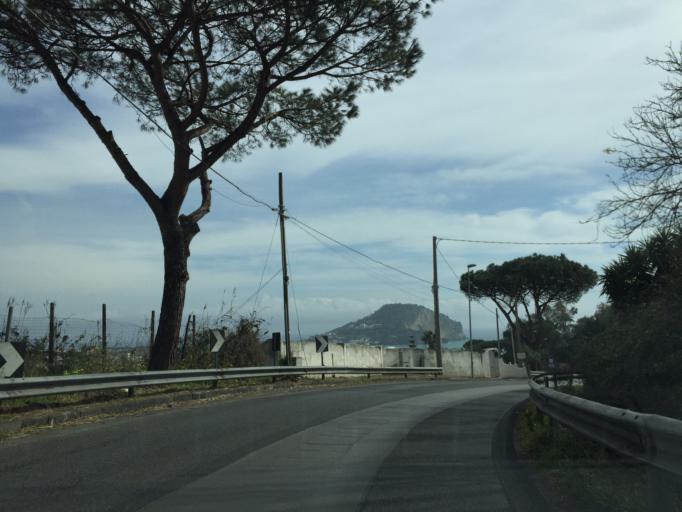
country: IT
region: Campania
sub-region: Provincia di Napoli
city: Monte di Procida
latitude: 40.7947
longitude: 14.0621
